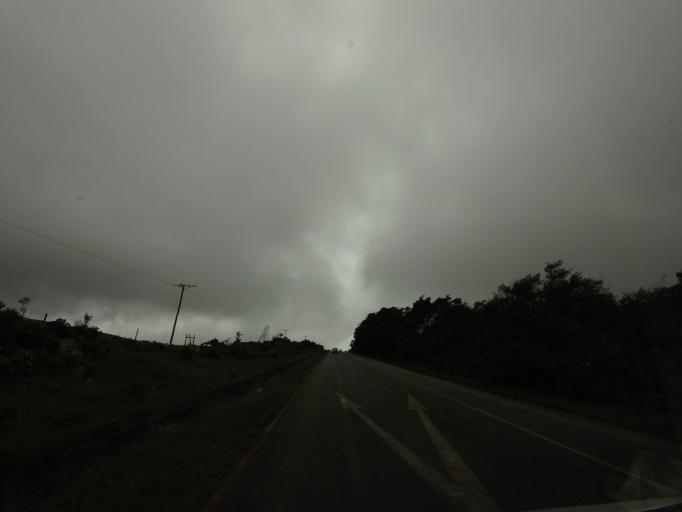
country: SZ
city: Darkton
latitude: -26.1419
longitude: 31.1210
